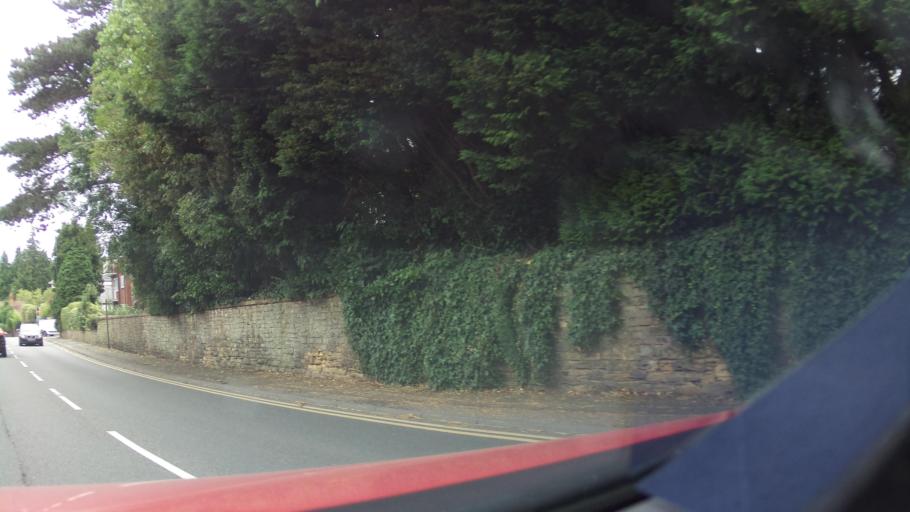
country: GB
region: England
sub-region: Worcestershire
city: Droitwich
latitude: 52.2656
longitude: -2.1491
